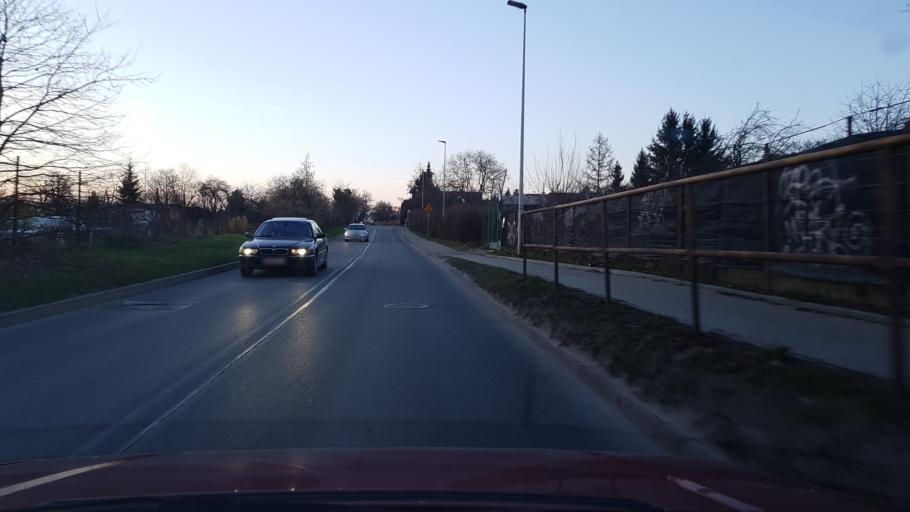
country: PL
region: West Pomeranian Voivodeship
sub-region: Szczecin
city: Szczecin
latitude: 53.4651
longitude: 14.5534
